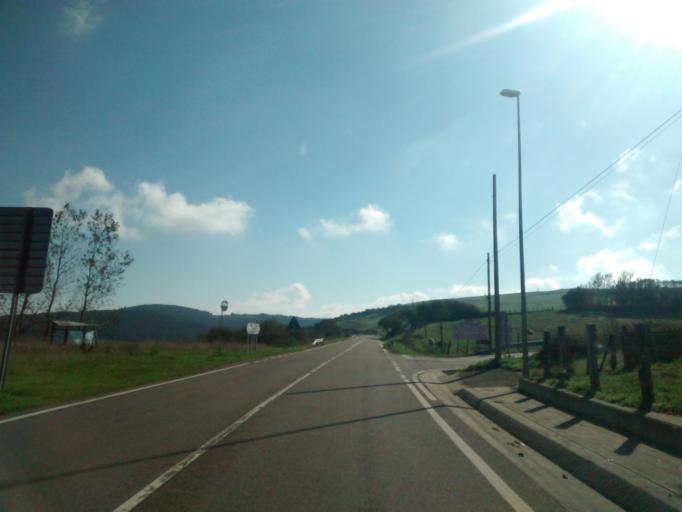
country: ES
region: Cantabria
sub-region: Provincia de Cantabria
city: Reinosa
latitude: 42.9907
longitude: -4.1184
